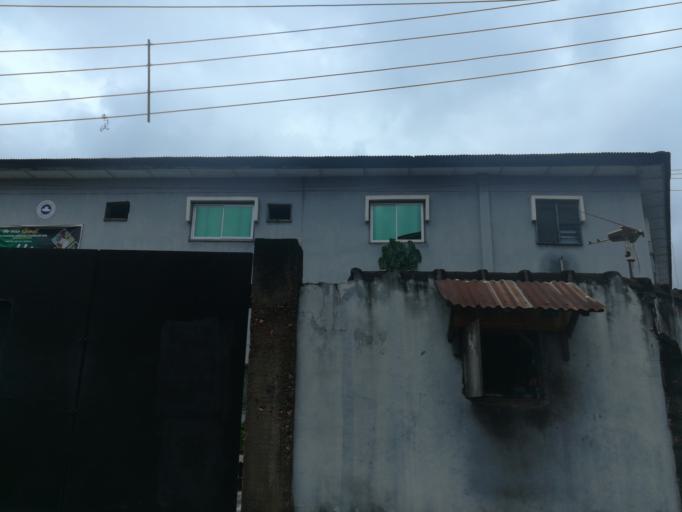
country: NG
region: Lagos
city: Ojota
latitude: 6.5709
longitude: 3.3713
